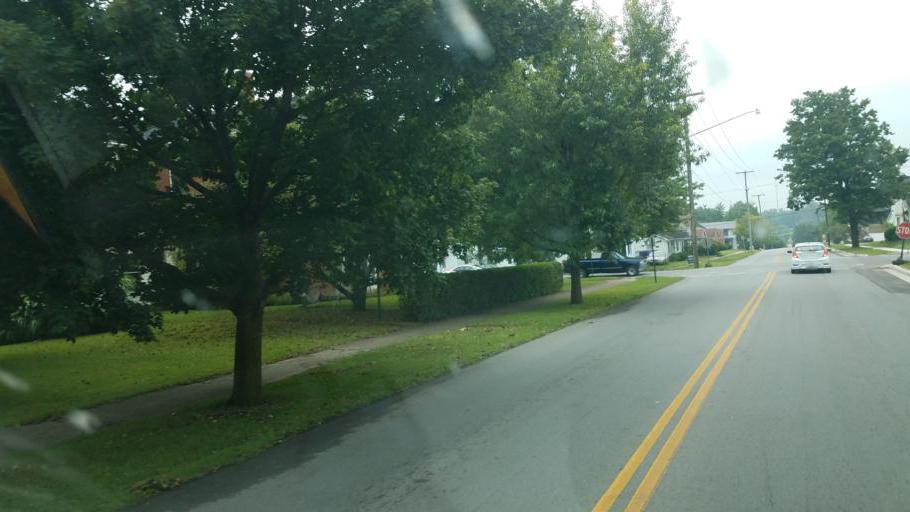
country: US
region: Ohio
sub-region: Highland County
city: Hillsboro
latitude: 39.2010
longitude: -83.6093
